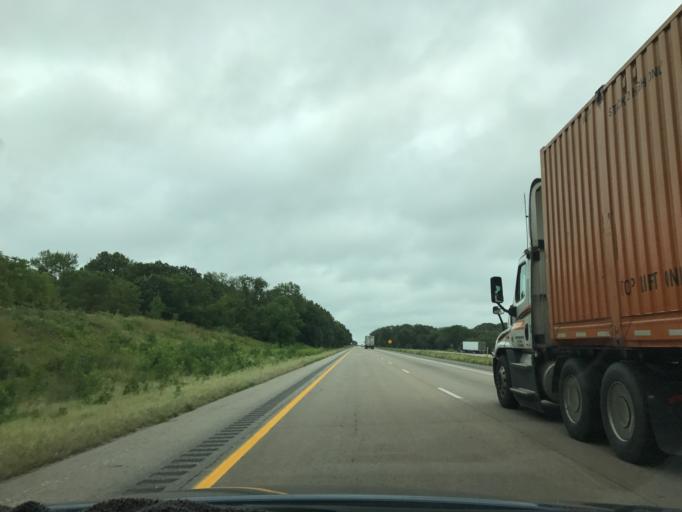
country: US
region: Iowa
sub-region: Muscatine County
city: Wilton
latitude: 41.6402
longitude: -91.0546
